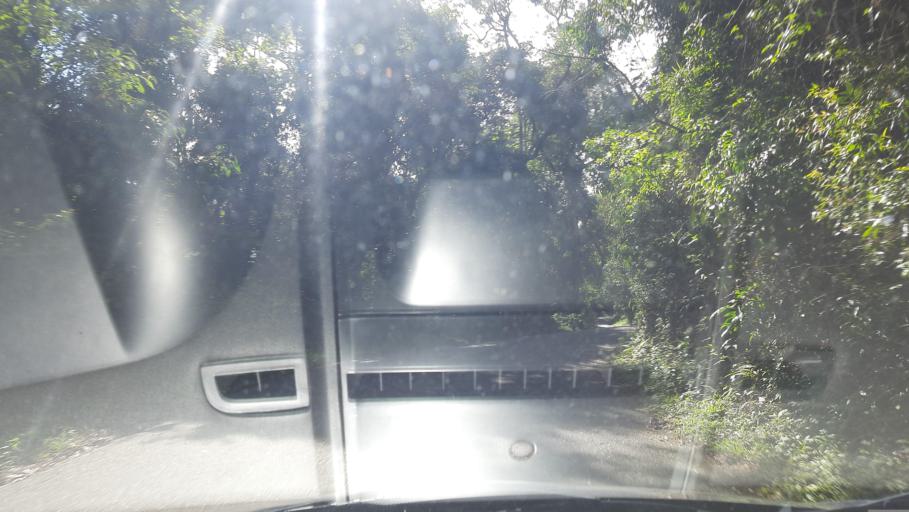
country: BR
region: Minas Gerais
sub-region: Pocos De Caldas
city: Pocos de Caldas
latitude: -21.7768
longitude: -46.5615
